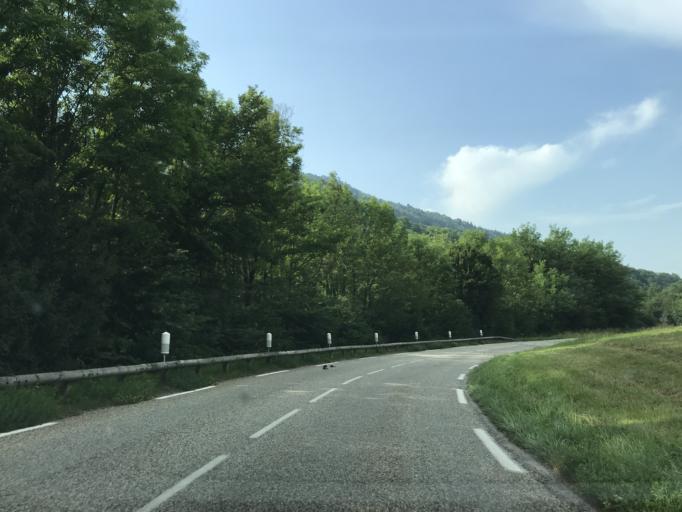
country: FR
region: Rhone-Alpes
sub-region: Departement de l'Isere
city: Allevard
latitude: 45.4113
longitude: 6.0860
